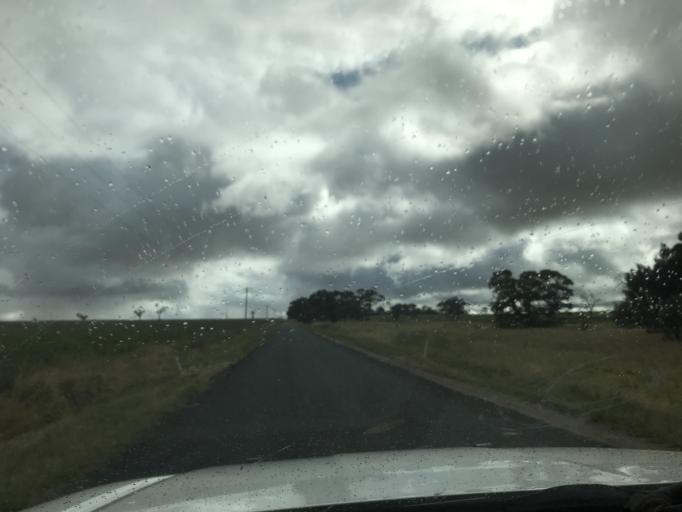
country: AU
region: South Australia
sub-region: Tatiara
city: Bordertown
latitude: -36.3585
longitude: 141.2720
